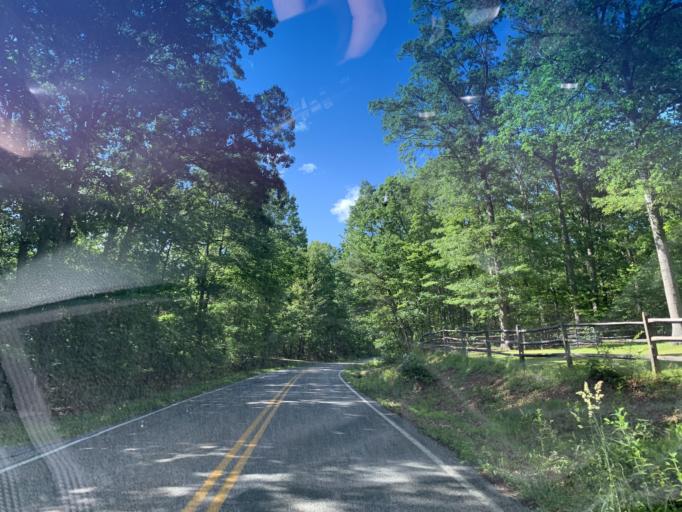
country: US
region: Maryland
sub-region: Cecil County
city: North East
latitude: 39.5540
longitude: -75.9240
